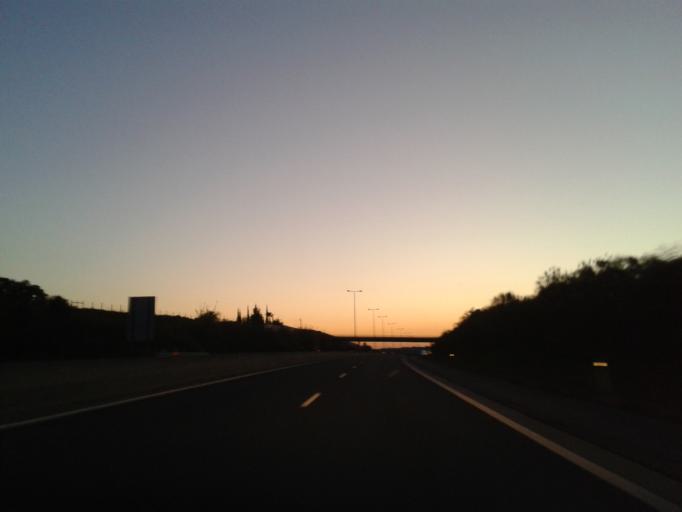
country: PT
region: Faro
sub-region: Albufeira
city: Guia
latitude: 37.1395
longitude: -8.3306
